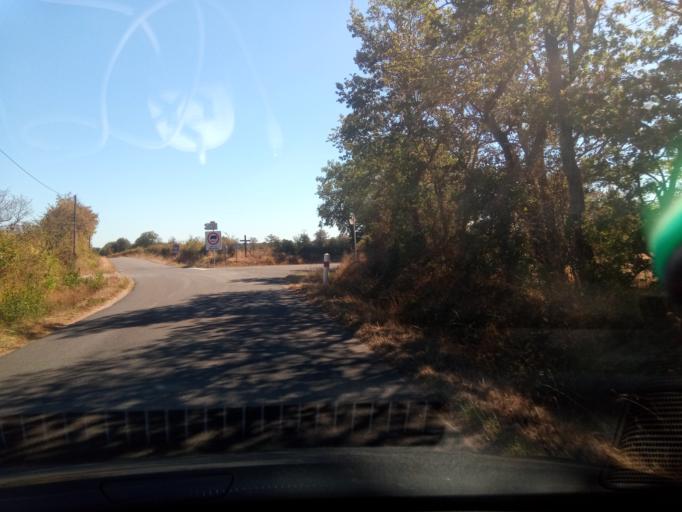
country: FR
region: Poitou-Charentes
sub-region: Departement de la Vienne
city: Saulge
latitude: 46.3787
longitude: 0.9017
